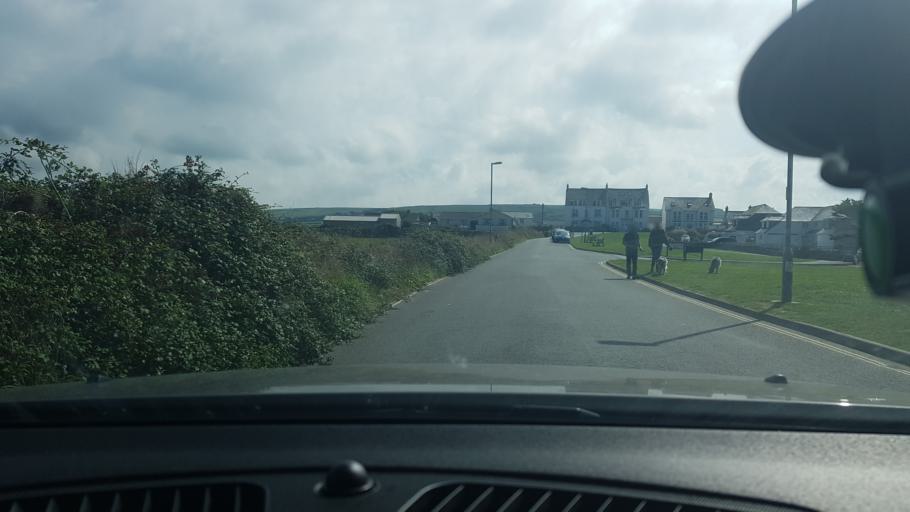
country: GB
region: England
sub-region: Cornwall
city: Tintagel
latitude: 50.6674
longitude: -4.7538
